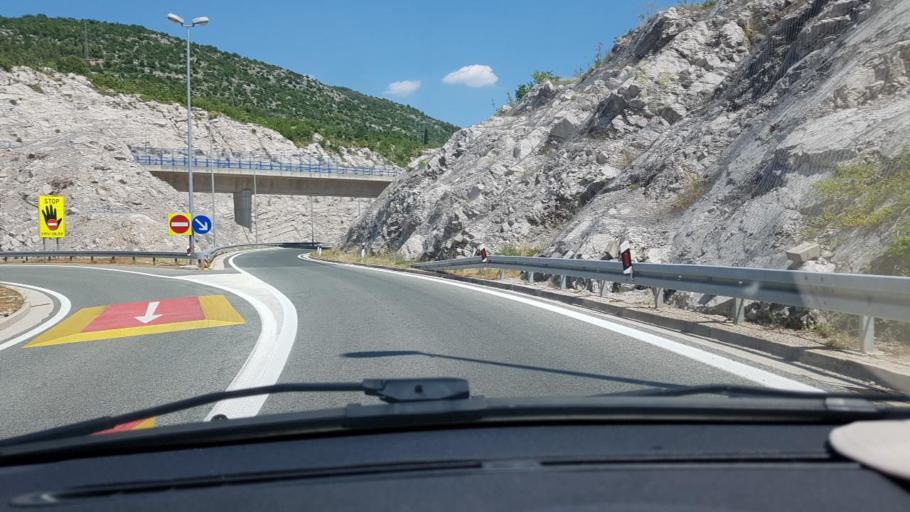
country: HR
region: Splitsko-Dalmatinska
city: Vrgorac
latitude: 43.1882
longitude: 17.3792
